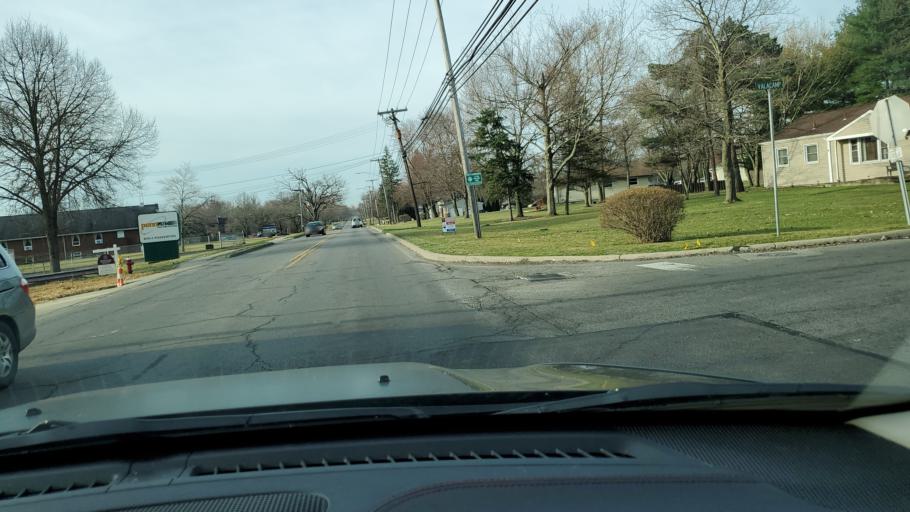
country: US
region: Ohio
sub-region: Trumbull County
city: Bolindale
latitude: 41.2101
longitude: -80.7637
